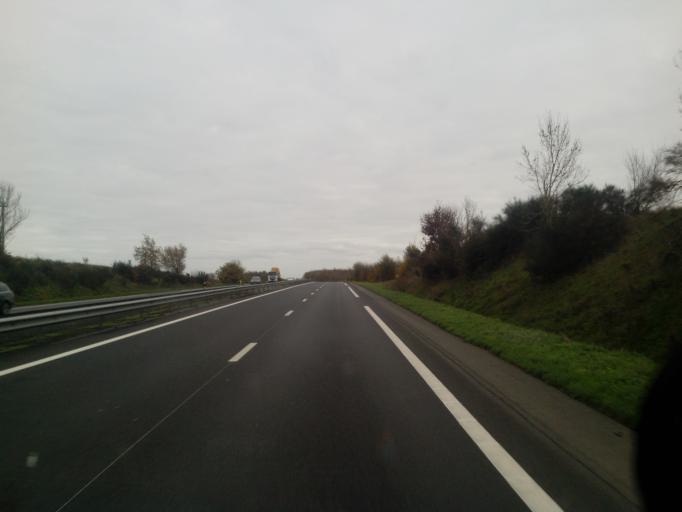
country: FR
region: Pays de la Loire
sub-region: Departement de Maine-et-Loire
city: Saint-Andre-de-la-Marche
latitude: 47.0973
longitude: -1.0147
